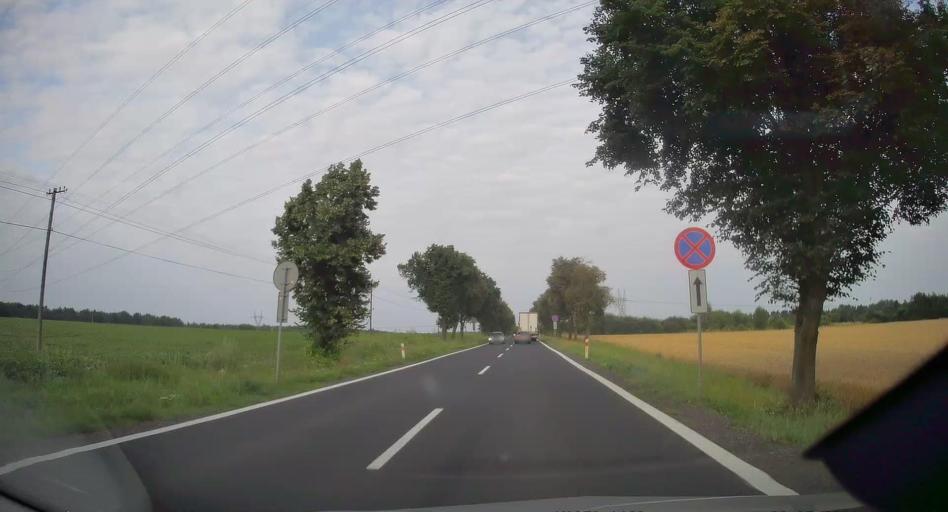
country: PL
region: Silesian Voivodeship
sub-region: Powiat czestochowski
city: Klomnice
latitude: 50.9145
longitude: 19.3214
